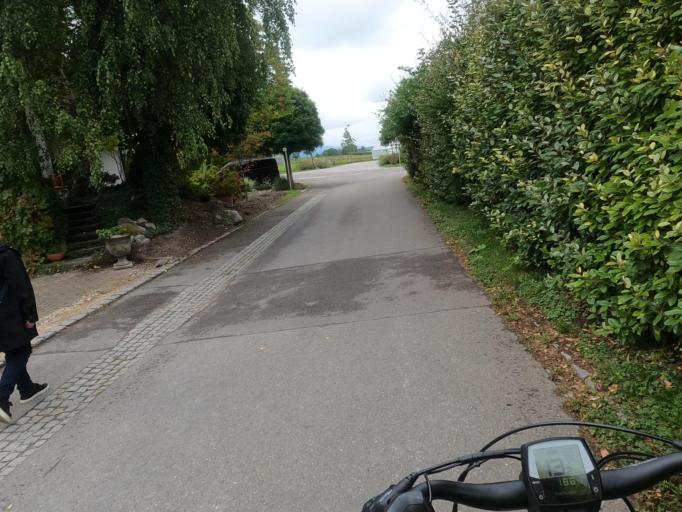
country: DE
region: Baden-Wuerttemberg
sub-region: Freiburg Region
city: Reichenau
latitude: 47.7009
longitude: 9.0599
